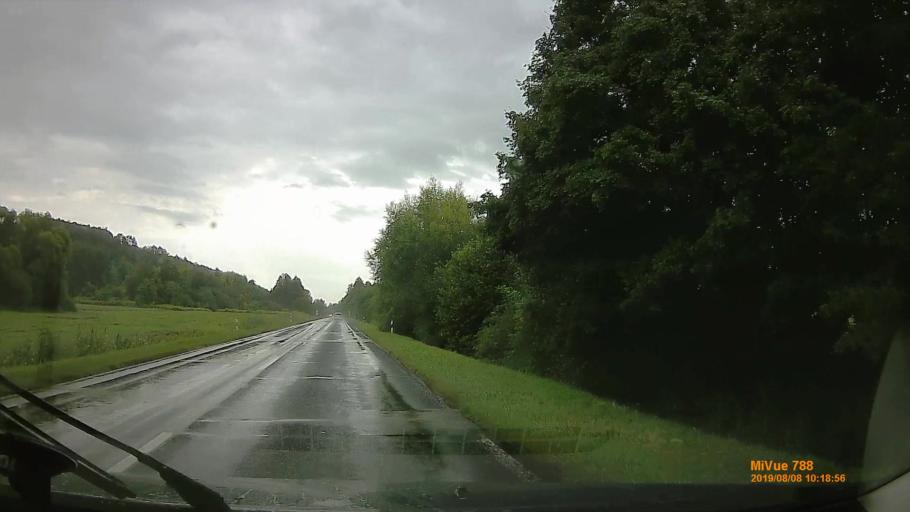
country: HU
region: Zala
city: Zalaegerszeg
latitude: 46.7700
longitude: 16.8580
